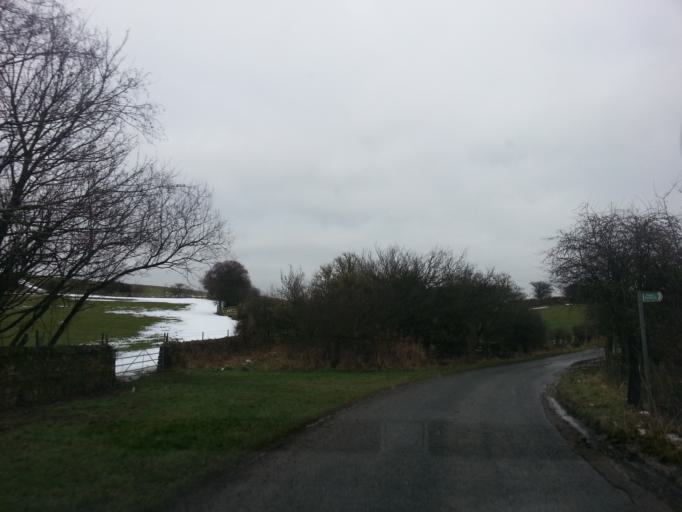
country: GB
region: England
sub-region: County Durham
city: Tow Law
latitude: 54.7751
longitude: -1.7794
